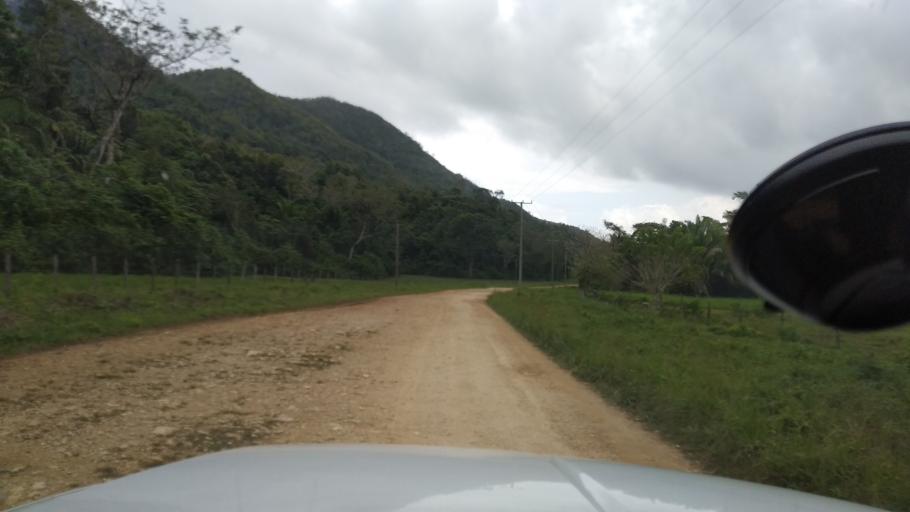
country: BZ
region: Toledo
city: Punta Gorda
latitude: 16.2105
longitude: -89.0229
